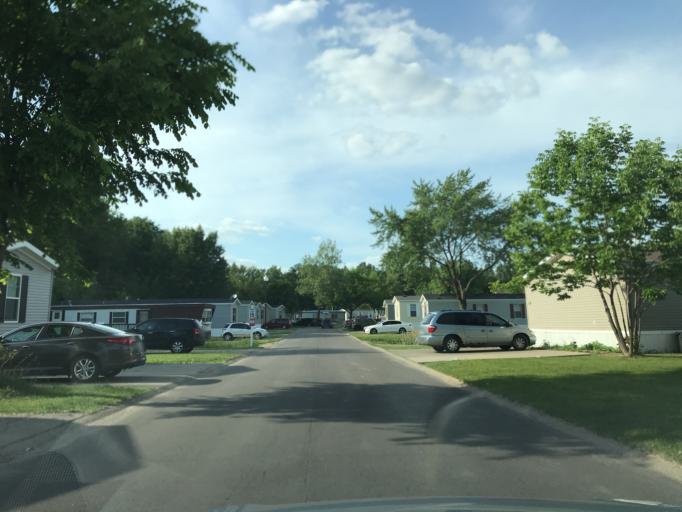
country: US
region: Michigan
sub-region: Oakland County
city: Walled Lake
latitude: 42.5152
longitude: -83.4646
